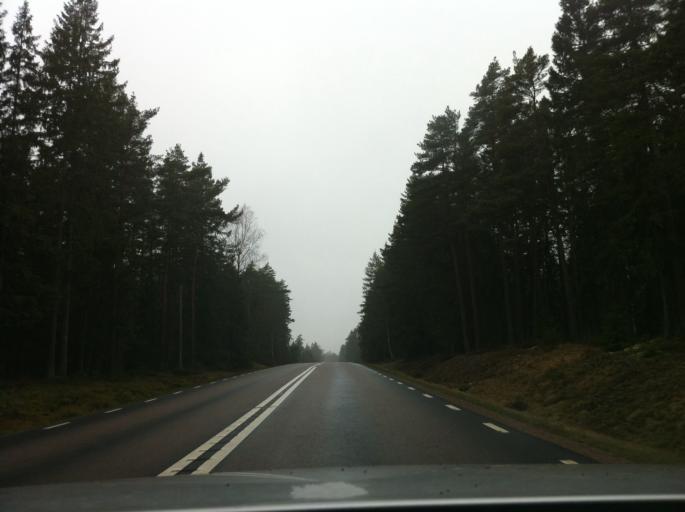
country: SE
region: Vaestra Goetaland
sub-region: Fargelanda Kommun
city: Faergelanda
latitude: 58.5252
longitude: 12.1539
